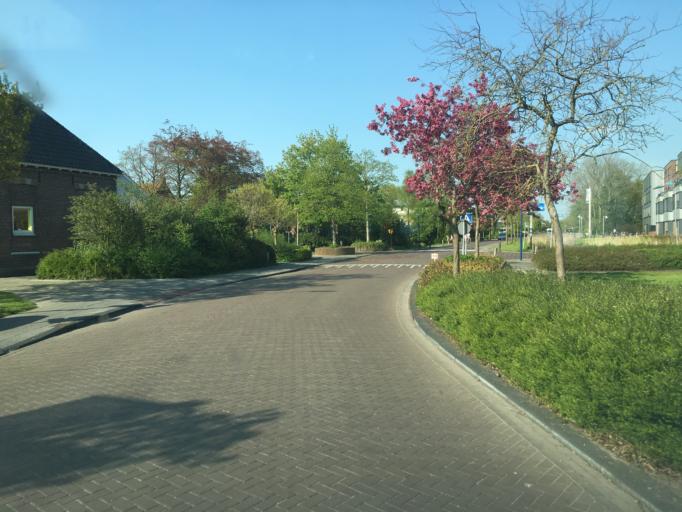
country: NL
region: Friesland
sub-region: Sudwest Fryslan
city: Workum
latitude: 52.9773
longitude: 5.4461
